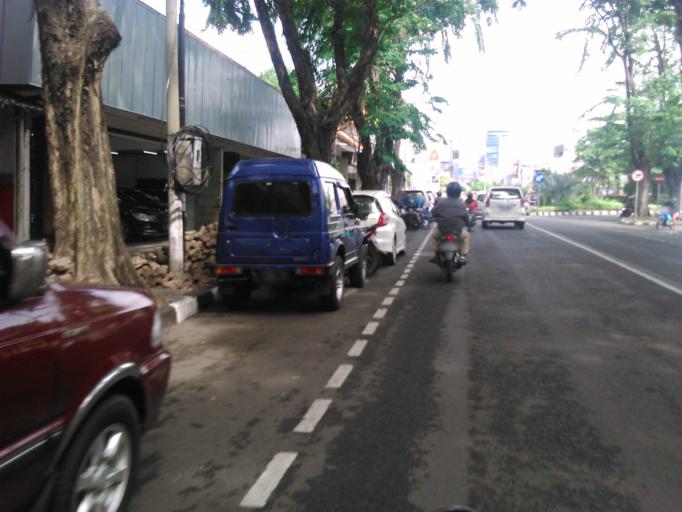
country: ID
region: East Java
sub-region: Kota Surabaya
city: Surabaya
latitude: -7.2599
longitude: 112.7440
